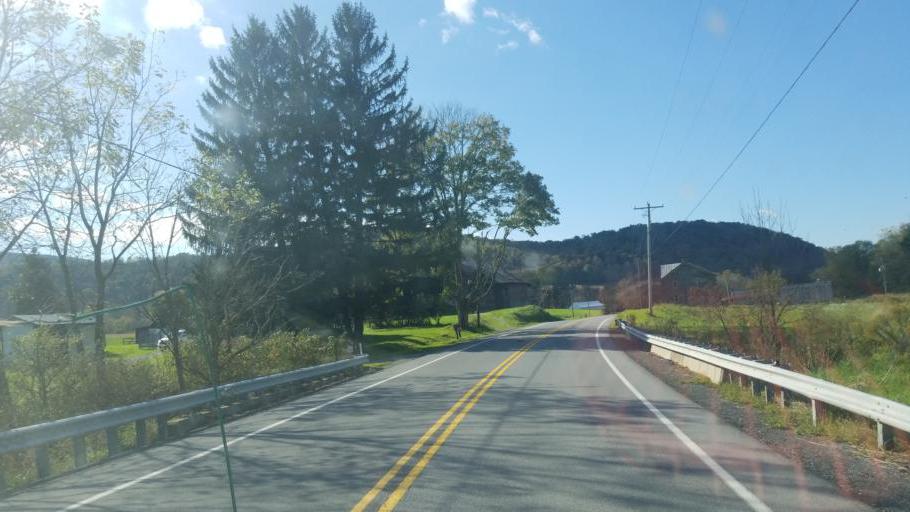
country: US
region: Pennsylvania
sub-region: Blair County
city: Claysburg
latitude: 40.1875
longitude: -78.4985
